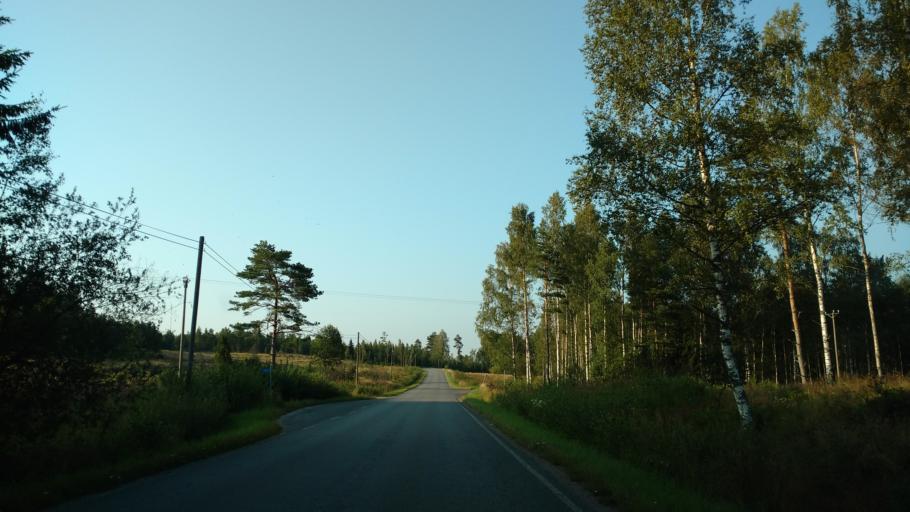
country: FI
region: Varsinais-Suomi
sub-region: Aboland-Turunmaa
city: Dragsfjaerd
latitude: 59.9365
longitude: 22.4137
